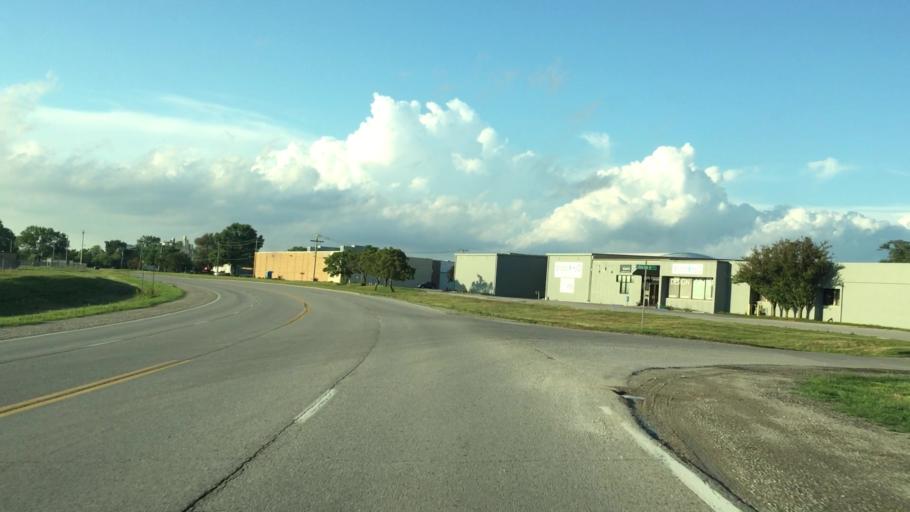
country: US
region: Iowa
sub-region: Johnson County
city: University Heights
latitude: 41.6340
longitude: -91.5390
